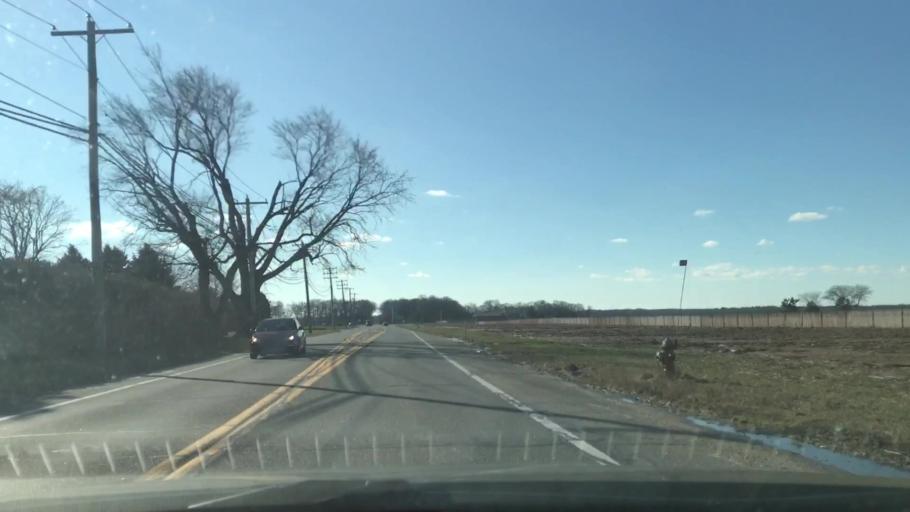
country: US
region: New York
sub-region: Suffolk County
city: Aquebogue
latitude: 40.9638
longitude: -72.6499
